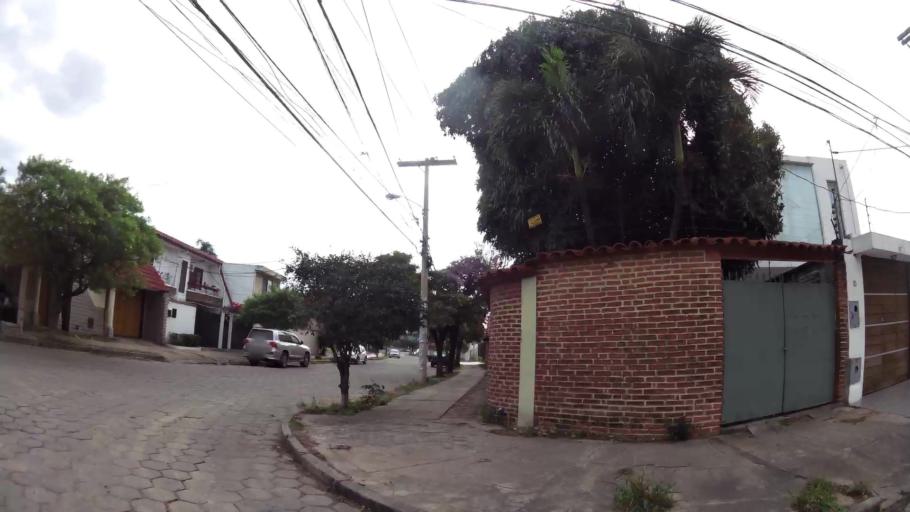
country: BO
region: Santa Cruz
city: Santa Cruz de la Sierra
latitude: -17.7754
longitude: -63.1903
